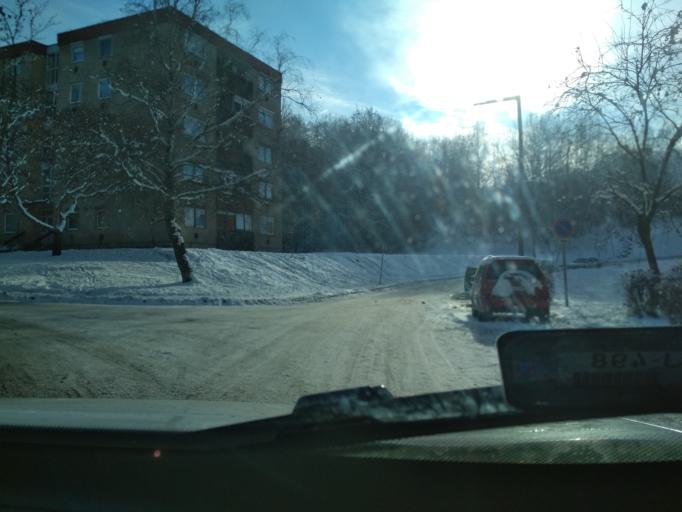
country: HU
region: Nograd
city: Salgotarjan
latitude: 48.1284
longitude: 19.8144
